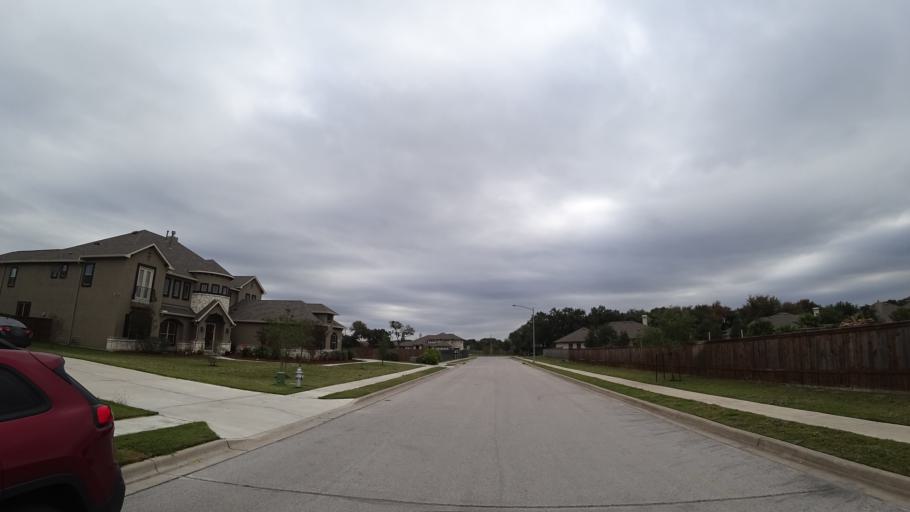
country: US
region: Texas
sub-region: Travis County
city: Shady Hollow
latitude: 30.1473
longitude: -97.8554
